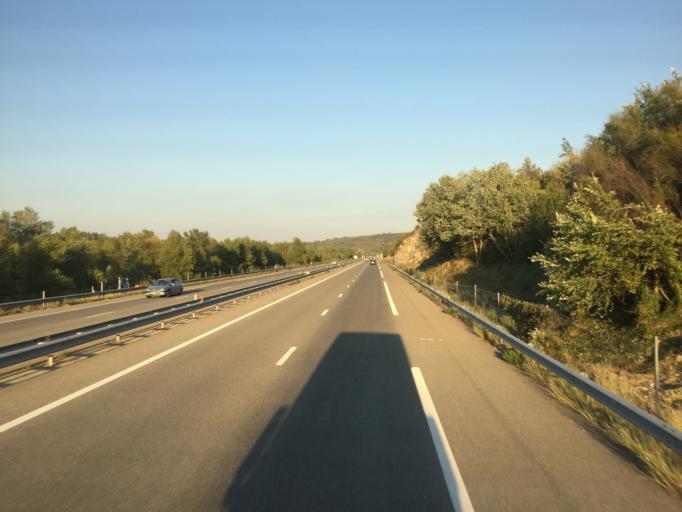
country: FR
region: Provence-Alpes-Cote d'Azur
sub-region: Departement du Vaucluse
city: Beaumont-de-Pertuis
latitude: 43.6902
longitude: 5.6898
